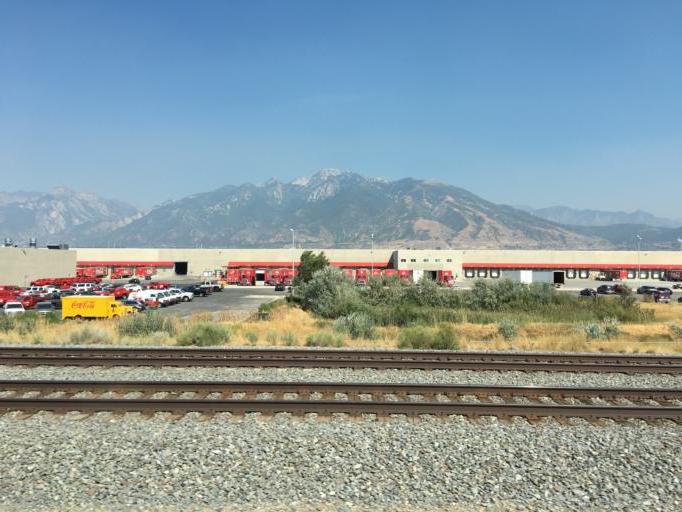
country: US
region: Utah
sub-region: Salt Lake County
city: Riverton
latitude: 40.5212
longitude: -111.9045
